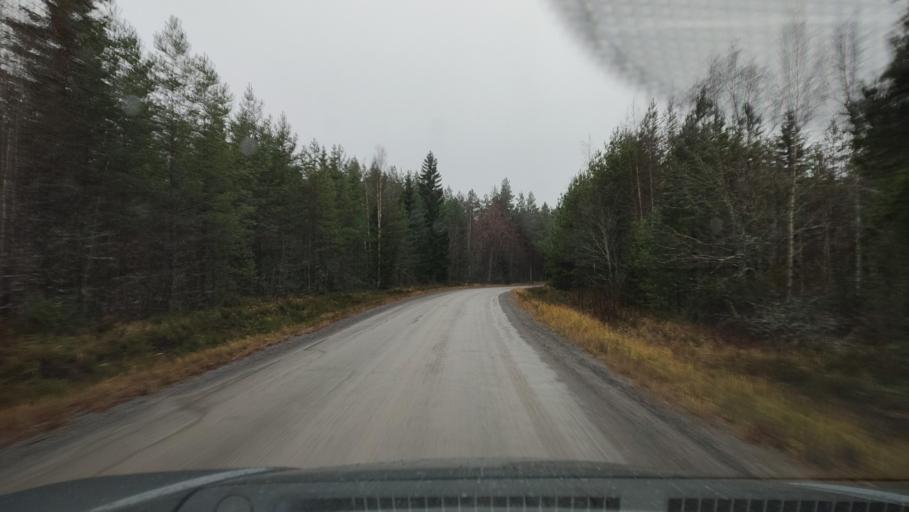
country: FI
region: Southern Ostrobothnia
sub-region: Suupohja
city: Karijoki
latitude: 62.1354
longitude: 21.6384
